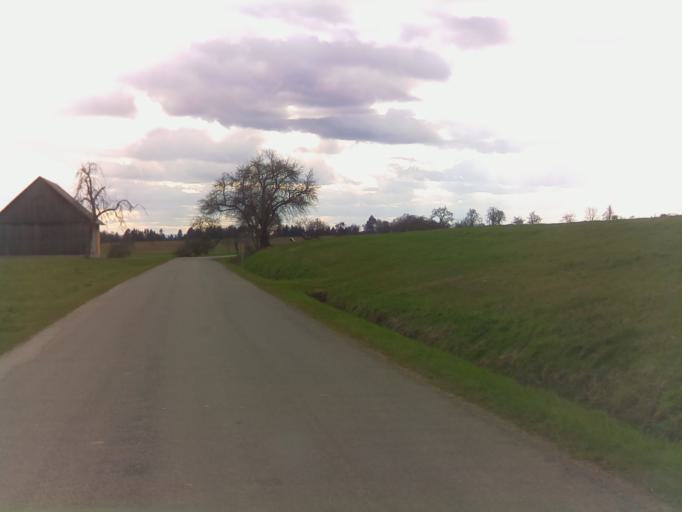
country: DE
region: Baden-Wuerttemberg
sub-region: Regierungsbezirk Stuttgart
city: Alfdorf
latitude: 48.8387
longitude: 9.6763
